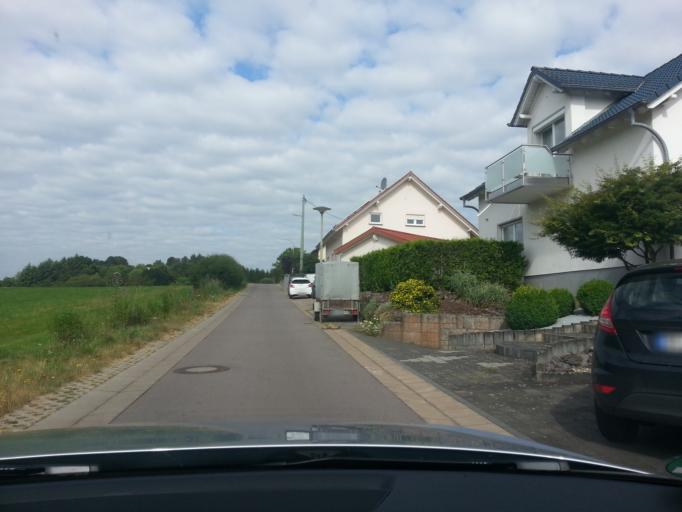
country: DE
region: Saarland
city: Schmelz
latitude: 49.4638
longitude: 6.8350
